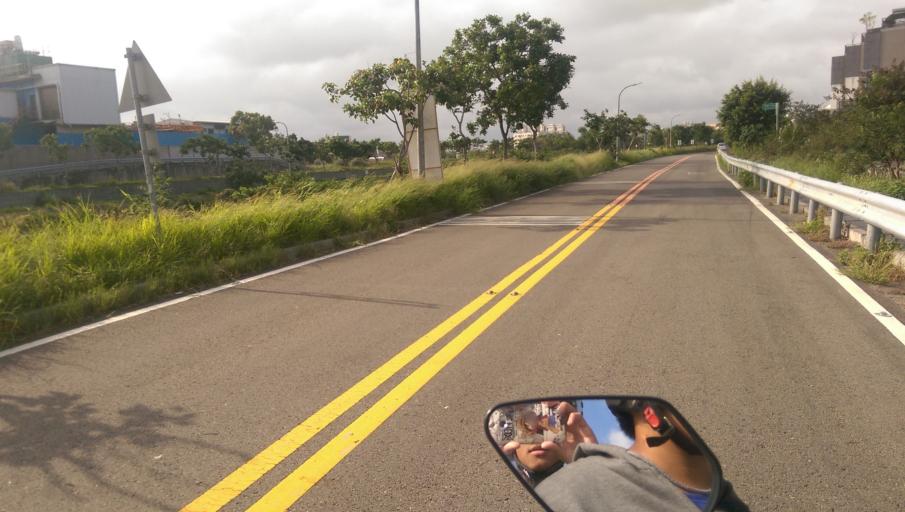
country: TW
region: Taiwan
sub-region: Hsinchu
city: Hsinchu
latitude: 24.8020
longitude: 120.9461
